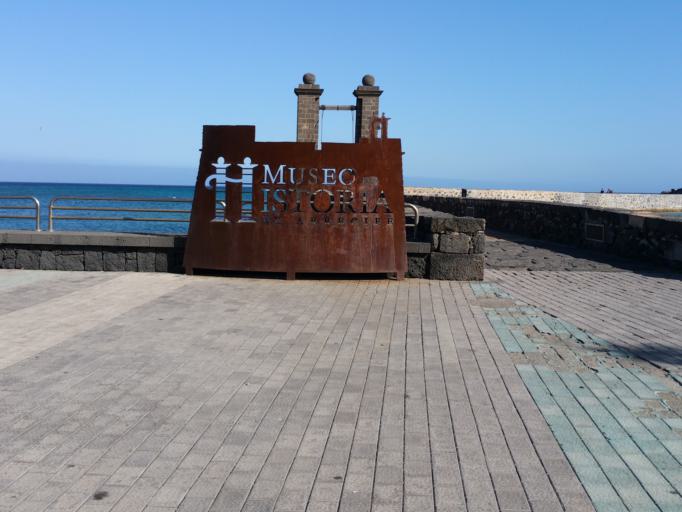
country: ES
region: Canary Islands
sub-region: Provincia de Las Palmas
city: Arrecife
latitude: 28.9586
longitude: -13.5478
